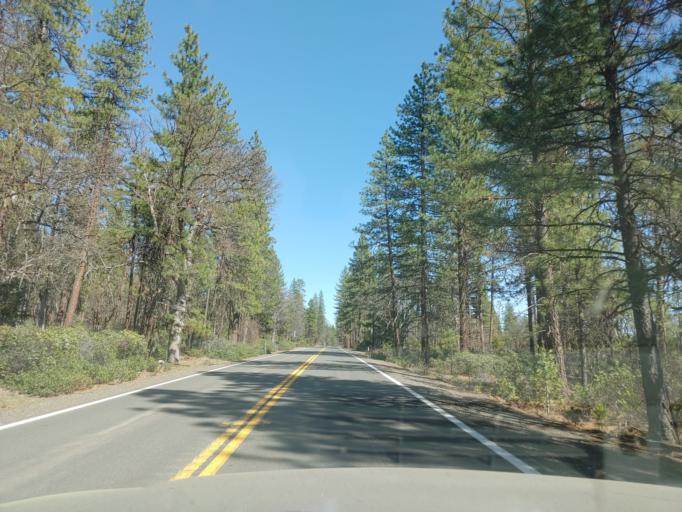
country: US
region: California
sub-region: Shasta County
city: Burney
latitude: 41.0084
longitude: -121.6443
